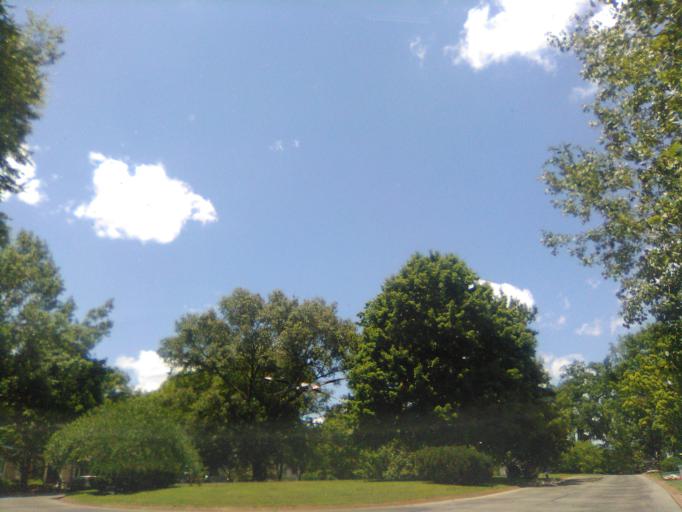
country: US
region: Tennessee
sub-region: Davidson County
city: Belle Meade
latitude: 36.1158
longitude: -86.8562
